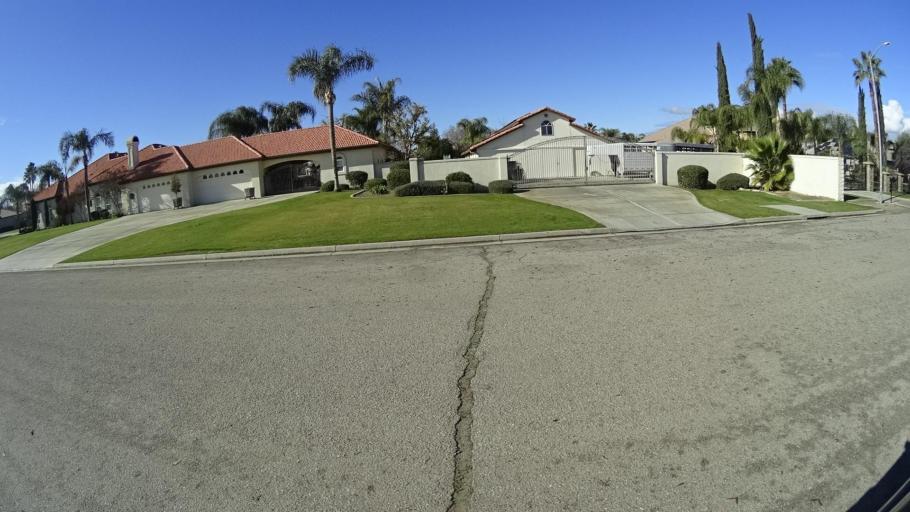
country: US
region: California
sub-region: Kern County
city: Rosedale
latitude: 35.3576
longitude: -119.1906
